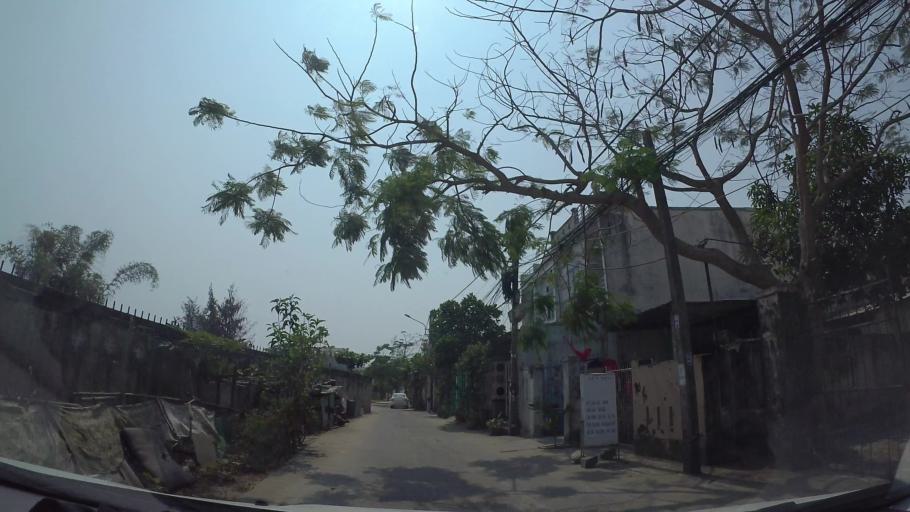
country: VN
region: Da Nang
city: Ngu Hanh Son
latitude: 16.0212
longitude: 108.2487
